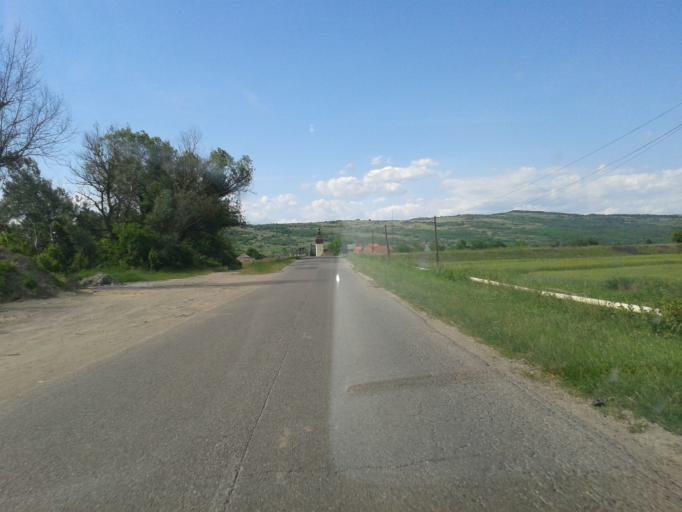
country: RO
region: Hunedoara
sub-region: Comuna Geoagiu
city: Geoagiu
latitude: 45.8977
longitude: 23.2256
